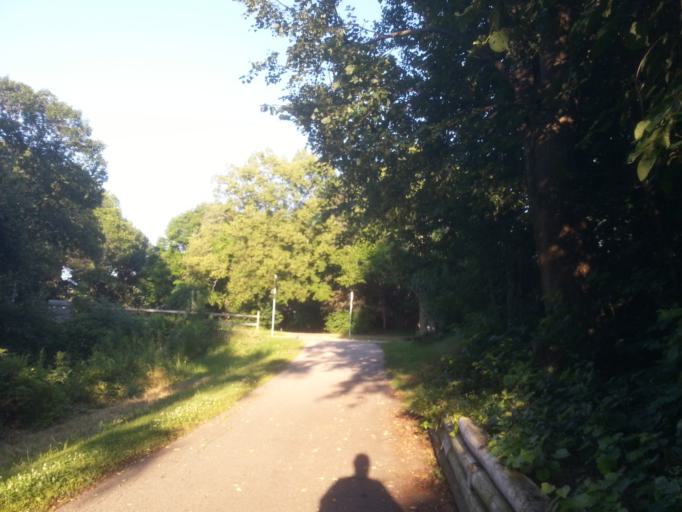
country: US
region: Wisconsin
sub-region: Dane County
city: Middleton
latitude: 43.0653
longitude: -89.4938
